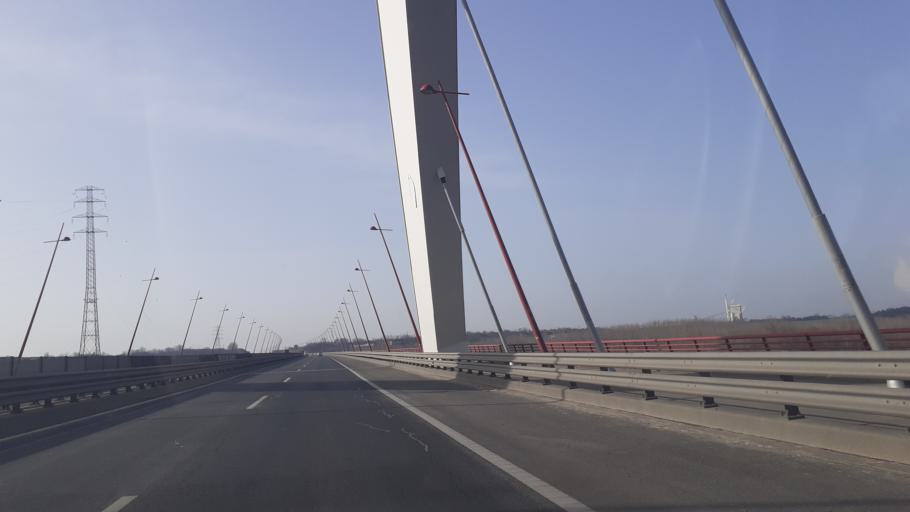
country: HU
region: Bacs-Kiskun
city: Dunavecse
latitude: 46.9035
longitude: 18.9581
